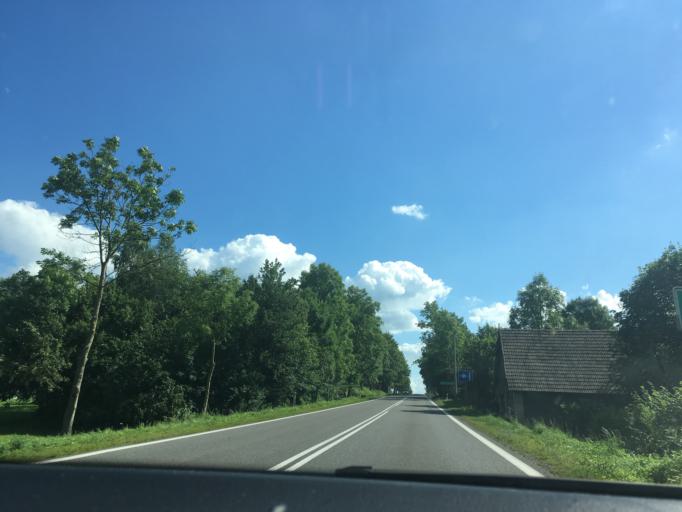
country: PL
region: Podlasie
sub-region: Powiat sokolski
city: Janow
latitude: 53.3942
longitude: 23.1142
